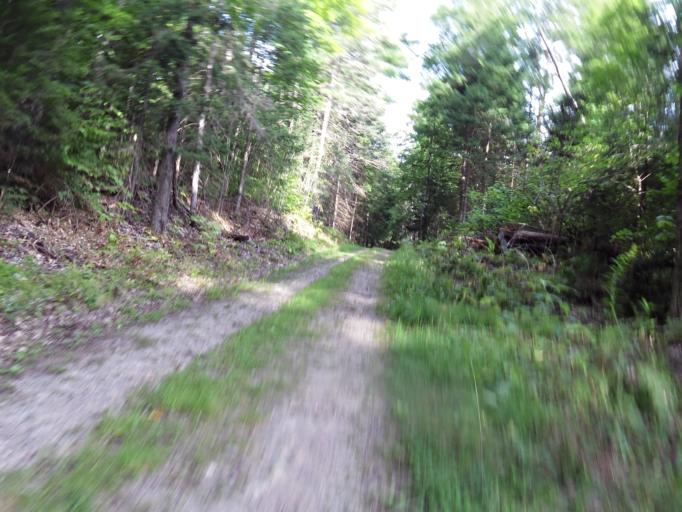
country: CA
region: Quebec
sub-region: Outaouais
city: Wakefield
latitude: 45.6275
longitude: -75.9740
